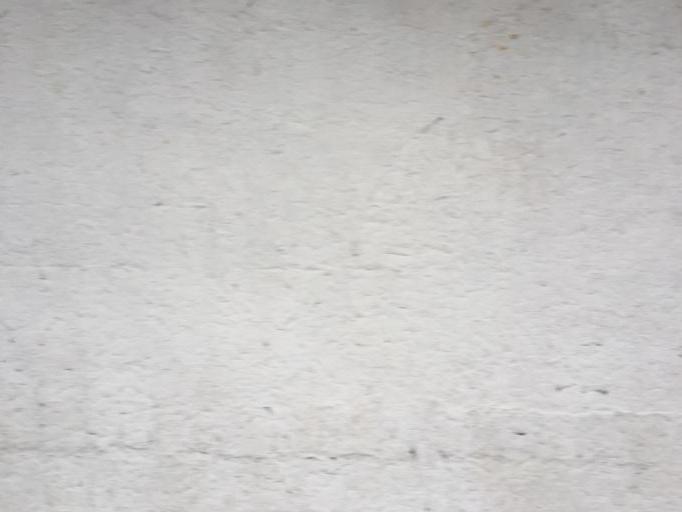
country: GT
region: Sacatepequez
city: Pastores
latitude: 14.5964
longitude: -90.7549
